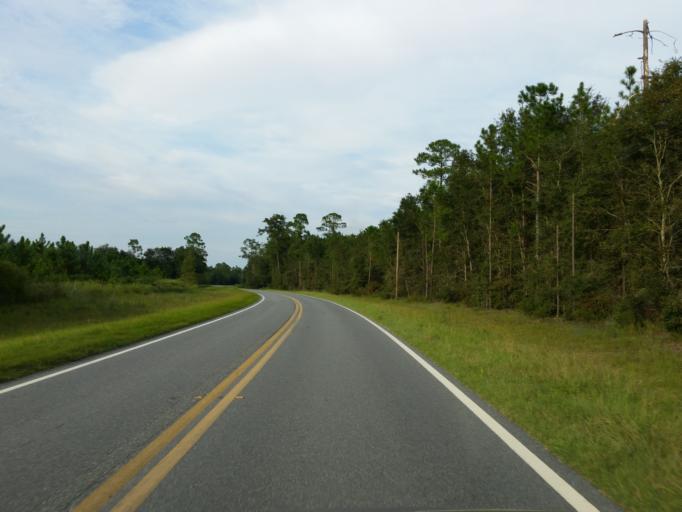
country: US
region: Georgia
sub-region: Echols County
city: Statenville
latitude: 30.5863
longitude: -83.1296
